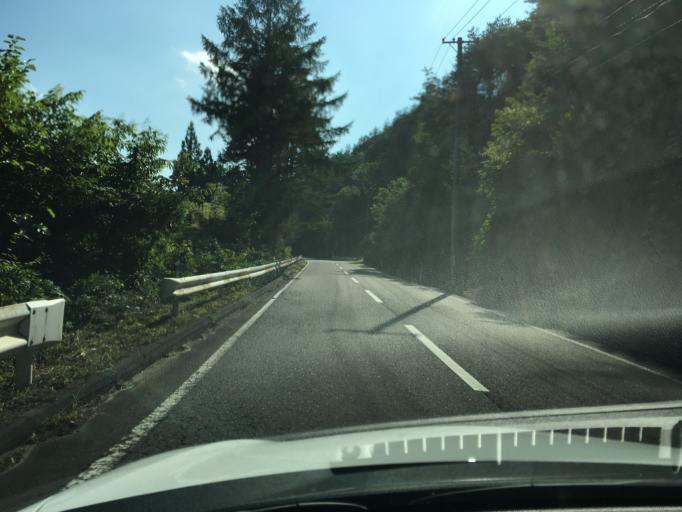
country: JP
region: Fukushima
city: Ishikawa
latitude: 37.2017
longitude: 140.5070
